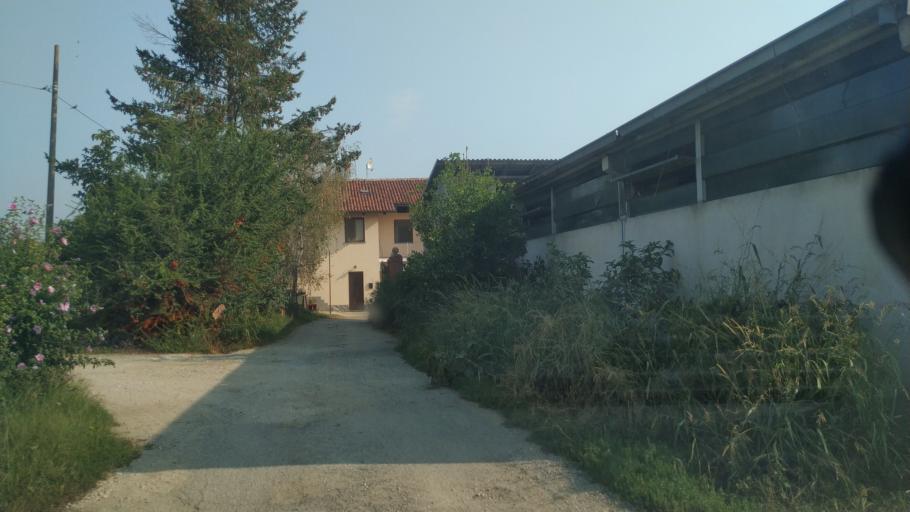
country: IT
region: Piedmont
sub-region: Provincia di Vercelli
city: Cigliano
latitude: 45.3263
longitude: 8.0283
